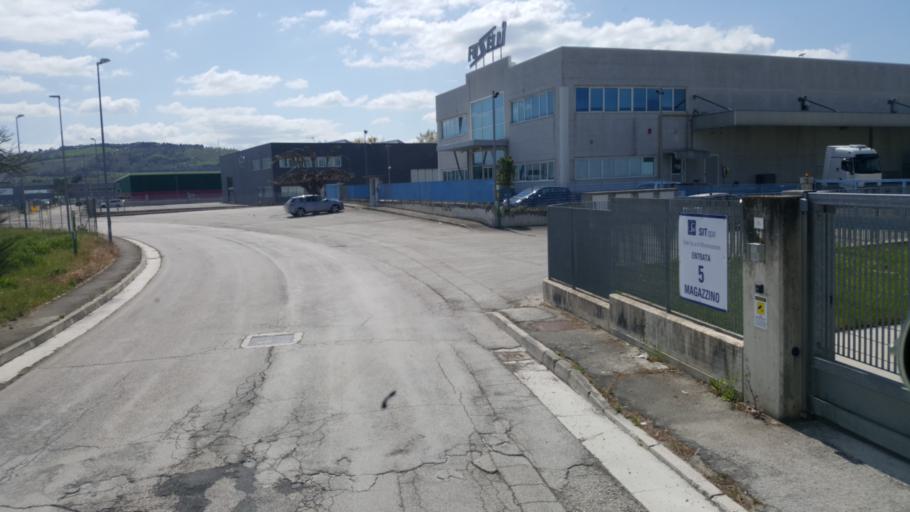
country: IT
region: The Marches
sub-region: Provincia di Macerata
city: Montecassiano
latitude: 43.3534
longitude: 13.4587
